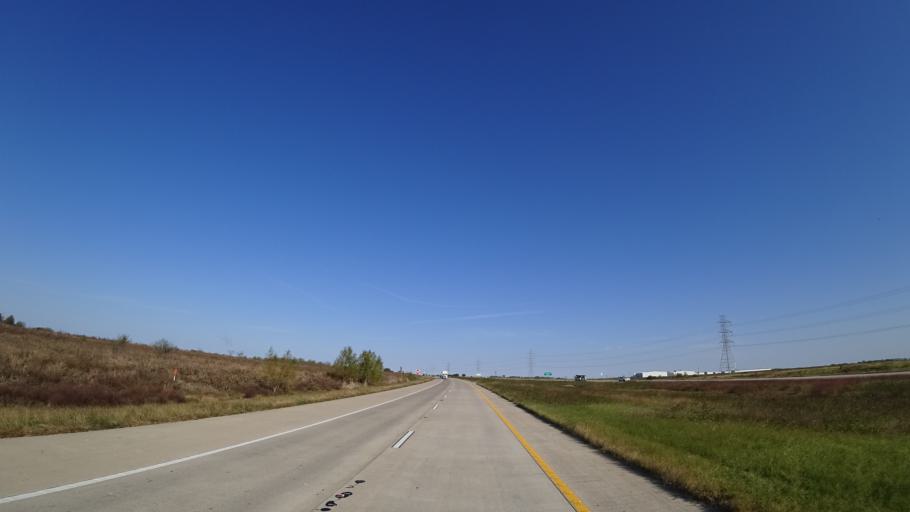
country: US
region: Texas
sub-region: Travis County
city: Manor
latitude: 30.3899
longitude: -97.5789
